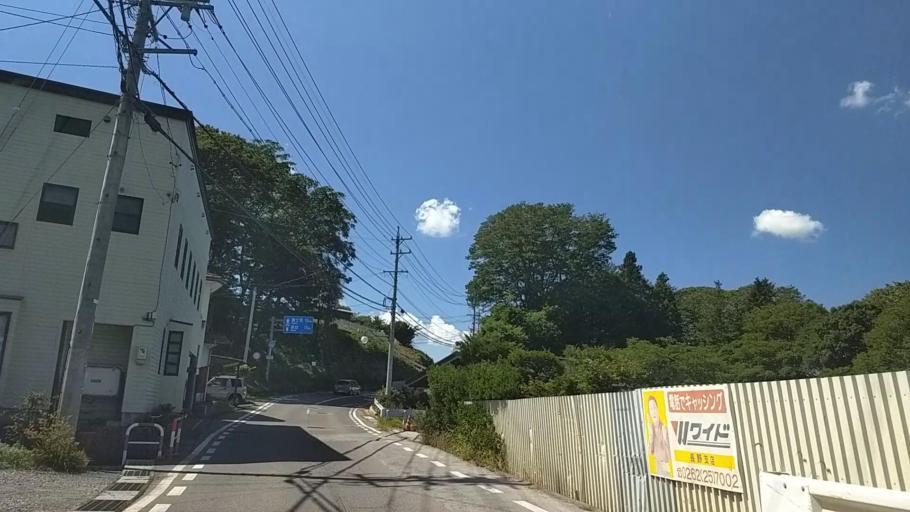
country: JP
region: Nagano
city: Chino
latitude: 36.0306
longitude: 138.2265
